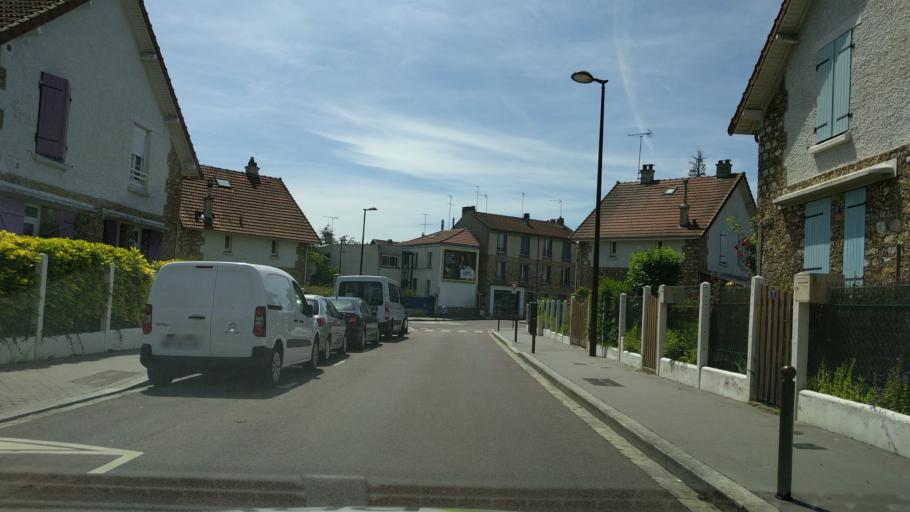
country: FR
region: Ile-de-France
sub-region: Departement des Yvelines
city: Viroflay
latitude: 48.8071
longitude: 2.1601
